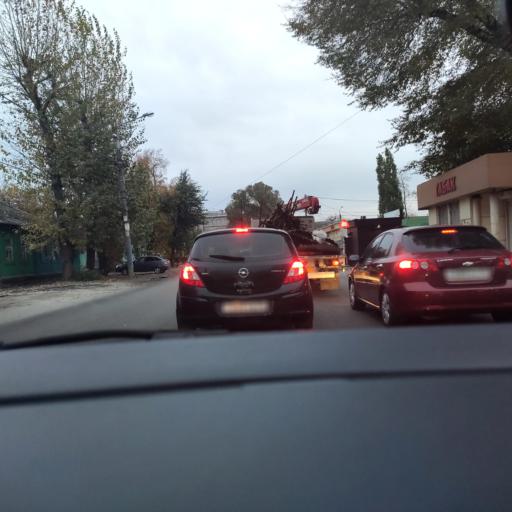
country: RU
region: Voronezj
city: Voronezh
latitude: 51.6348
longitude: 39.1890
